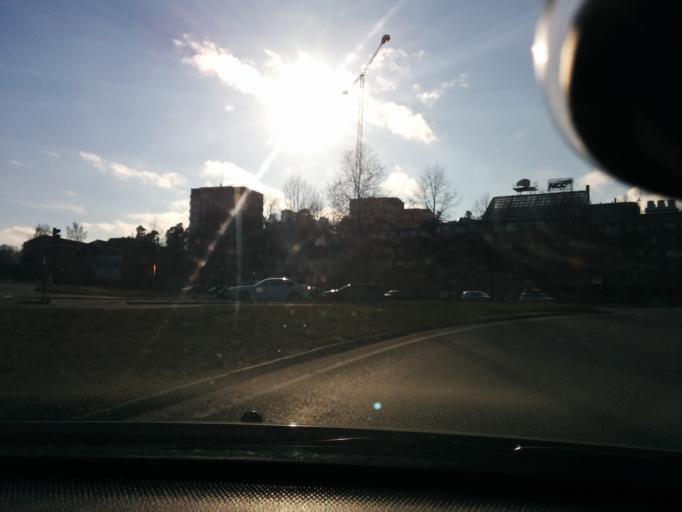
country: SE
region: Stockholm
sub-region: Solna Kommun
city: Solna
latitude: 59.3784
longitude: 18.0112
